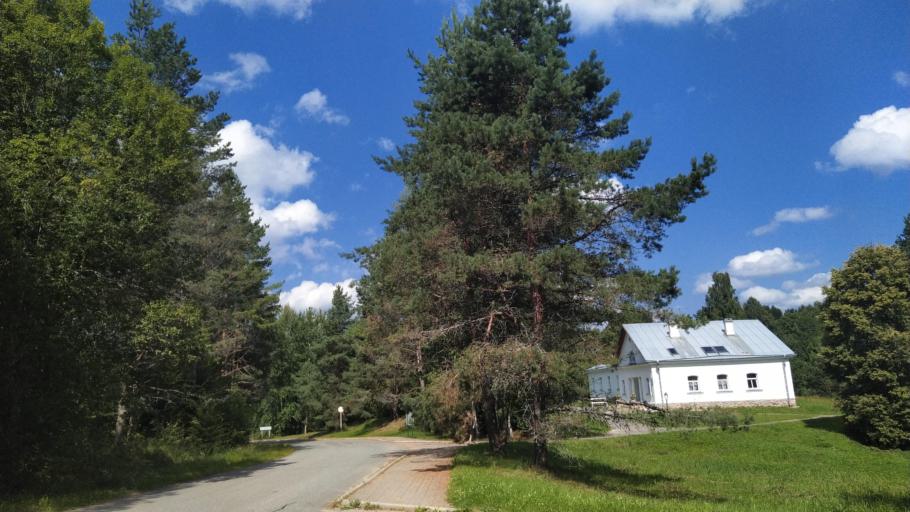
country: RU
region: Pskov
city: Pushkinskiye Gory
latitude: 57.0755
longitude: 28.9563
